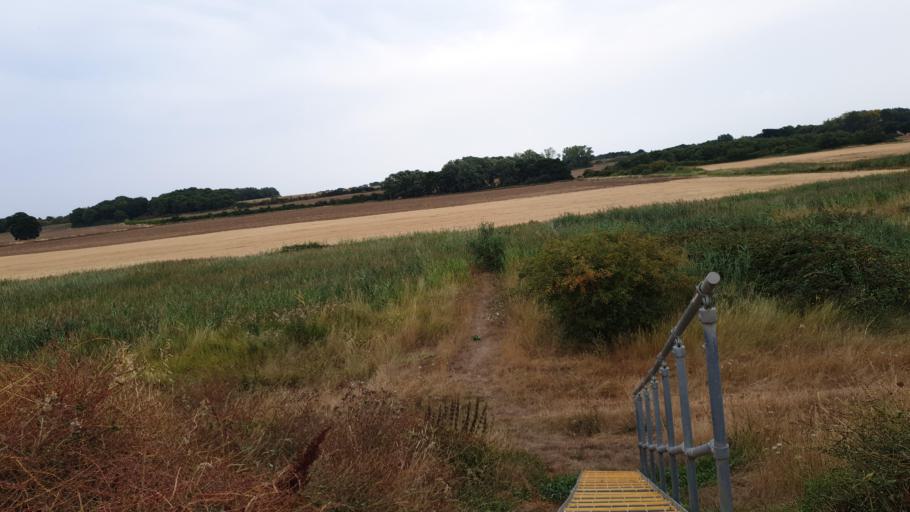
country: GB
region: England
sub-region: Essex
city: Brightlingsea
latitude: 51.8189
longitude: 0.9928
